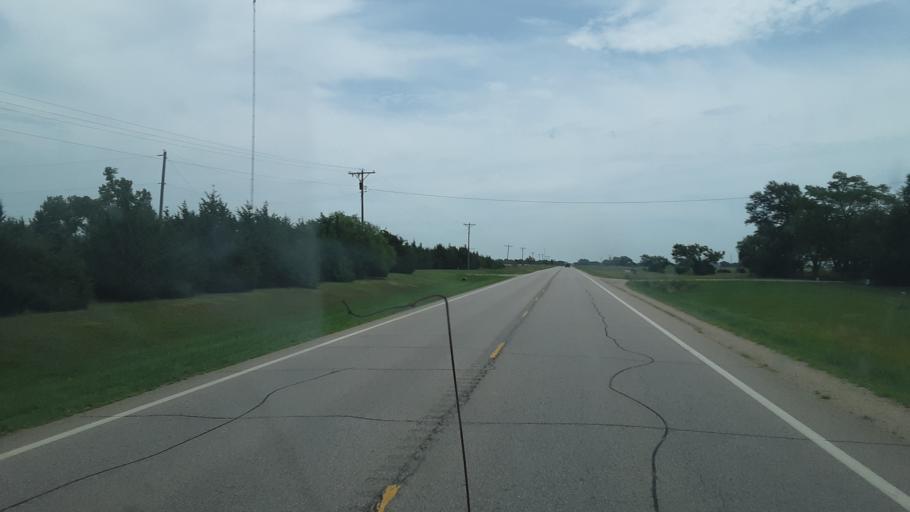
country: US
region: Kansas
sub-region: Butler County
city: El Dorado
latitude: 37.8106
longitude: -96.6479
